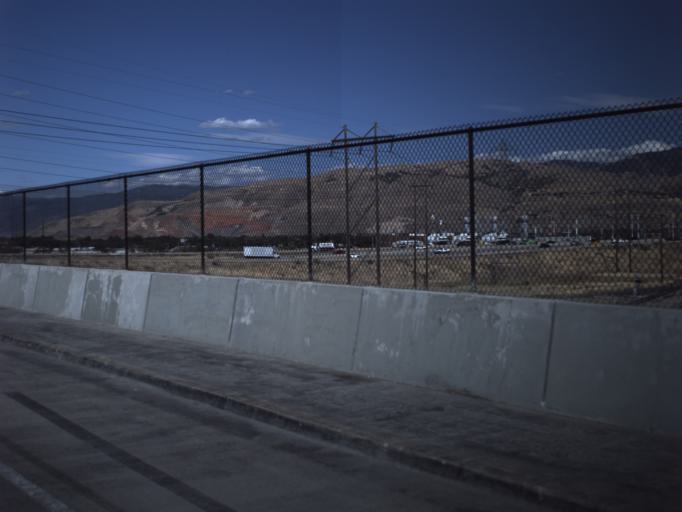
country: US
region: Utah
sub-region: Salt Lake County
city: Salt Lake City
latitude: 40.7639
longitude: -111.9390
